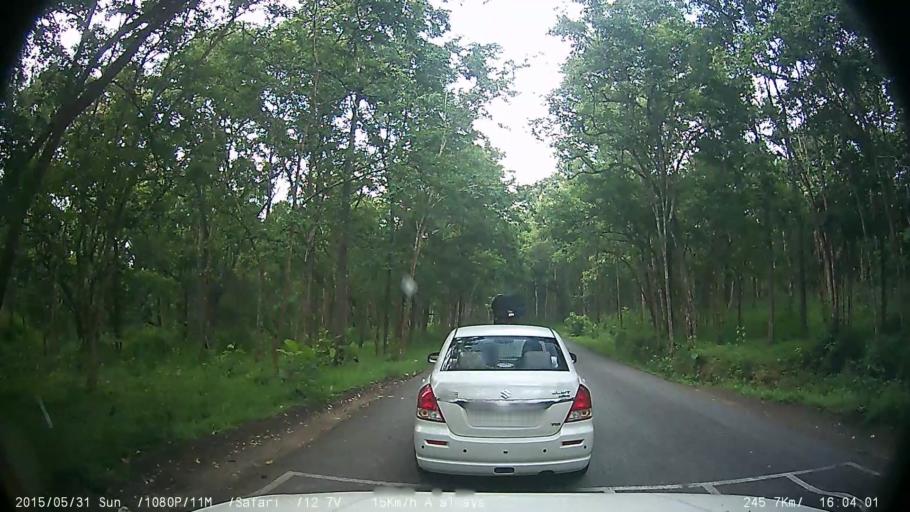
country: IN
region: Tamil Nadu
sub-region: Nilgiri
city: Naduvattam
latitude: 11.7083
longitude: 76.4141
